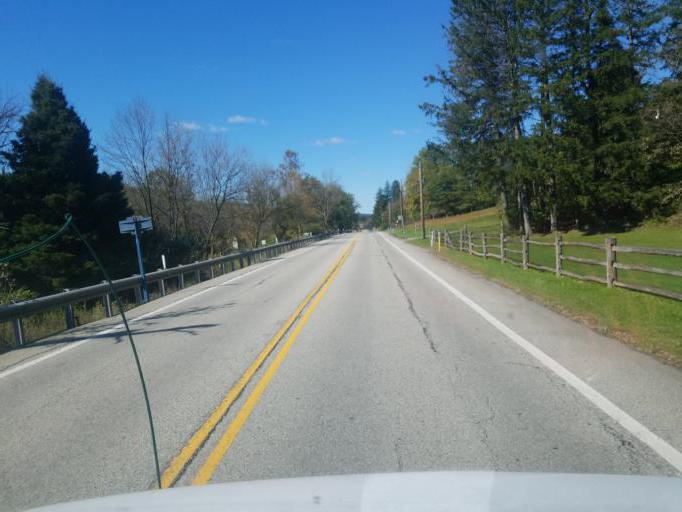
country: US
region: Pennsylvania
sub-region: Westmoreland County
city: Ligonier
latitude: 40.2140
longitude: -79.2026
